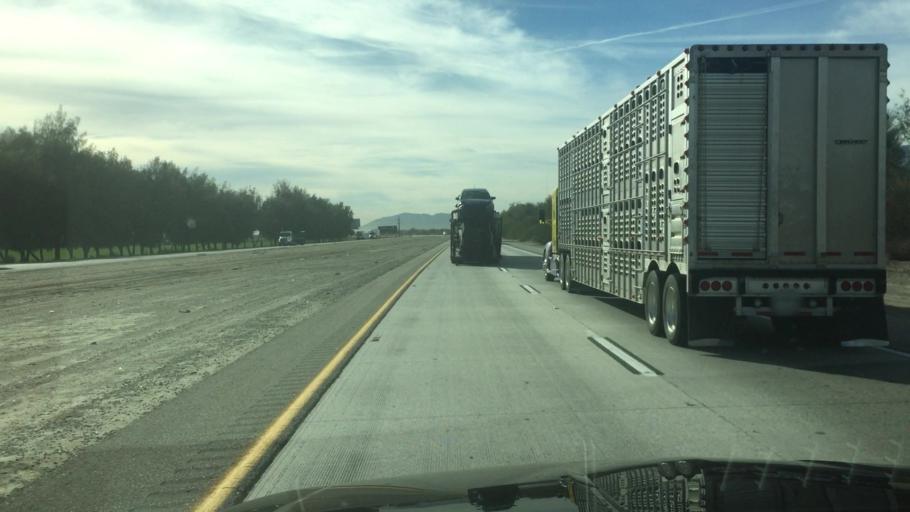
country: US
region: California
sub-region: Riverside County
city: Thermal
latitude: 33.6644
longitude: -116.1428
